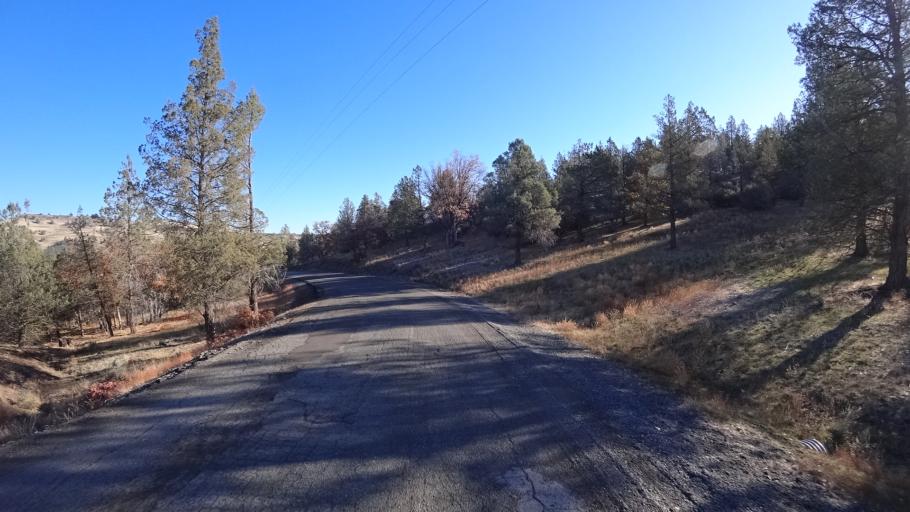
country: US
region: California
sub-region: Siskiyou County
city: Montague
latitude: 41.8868
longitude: -122.4432
